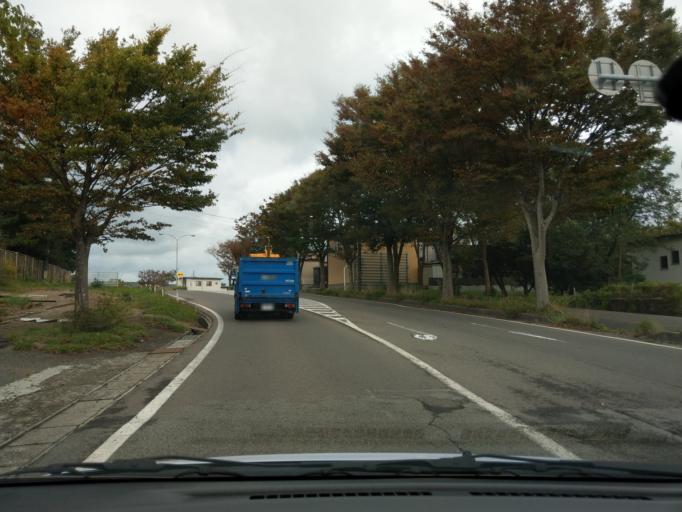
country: JP
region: Akita
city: Akita Shi
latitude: 39.6782
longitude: 140.0779
